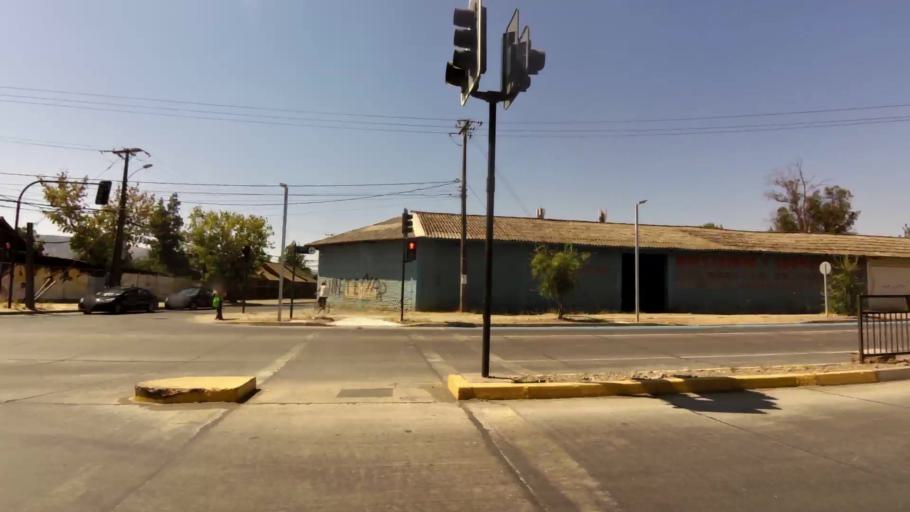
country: CL
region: Maule
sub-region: Provincia de Talca
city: Talca
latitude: -35.4116
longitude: -71.6582
